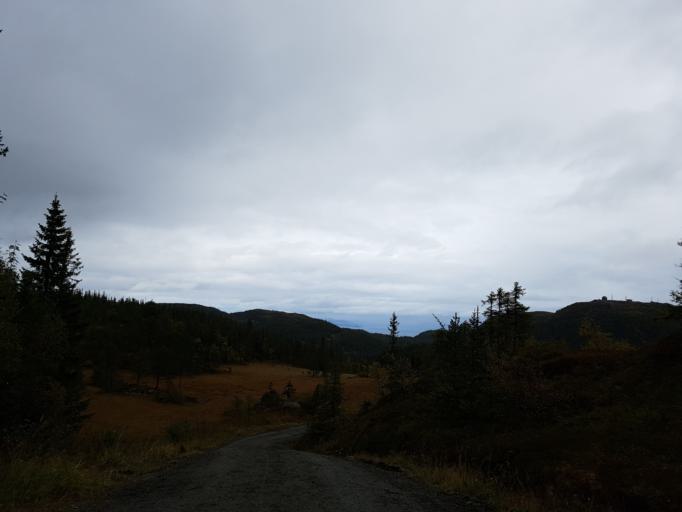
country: NO
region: Sor-Trondelag
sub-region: Melhus
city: Melhus
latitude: 63.4188
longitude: 10.2117
